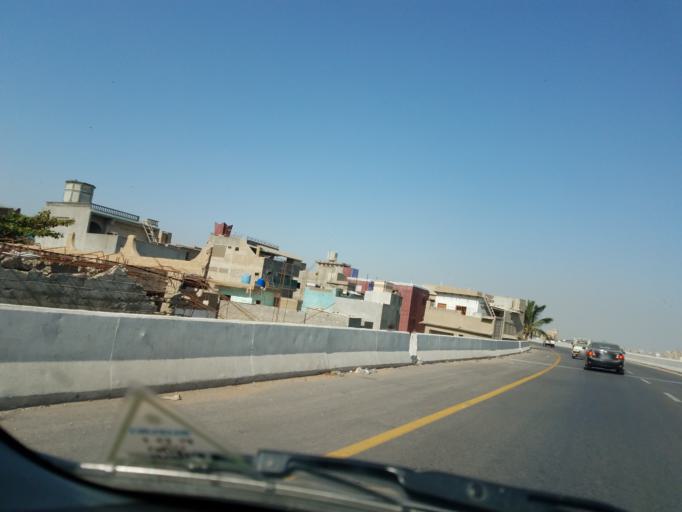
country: PK
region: Sindh
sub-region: Karachi District
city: Karachi
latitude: 24.8808
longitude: 67.0168
